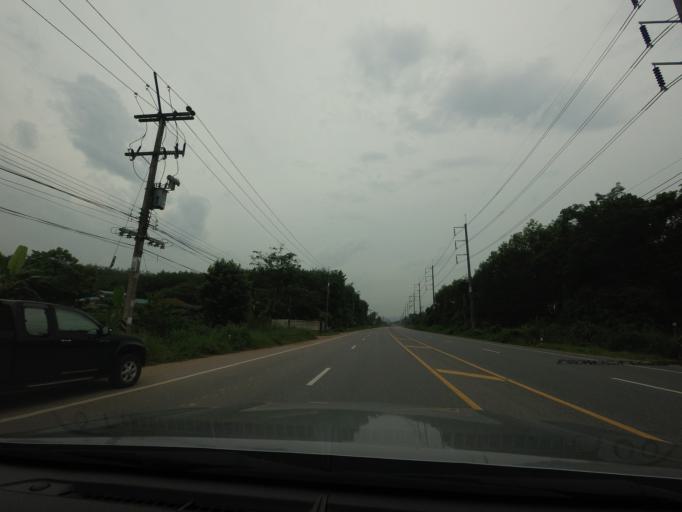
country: TH
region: Songkhla
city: Na Mom
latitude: 7.0546
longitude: 100.6485
